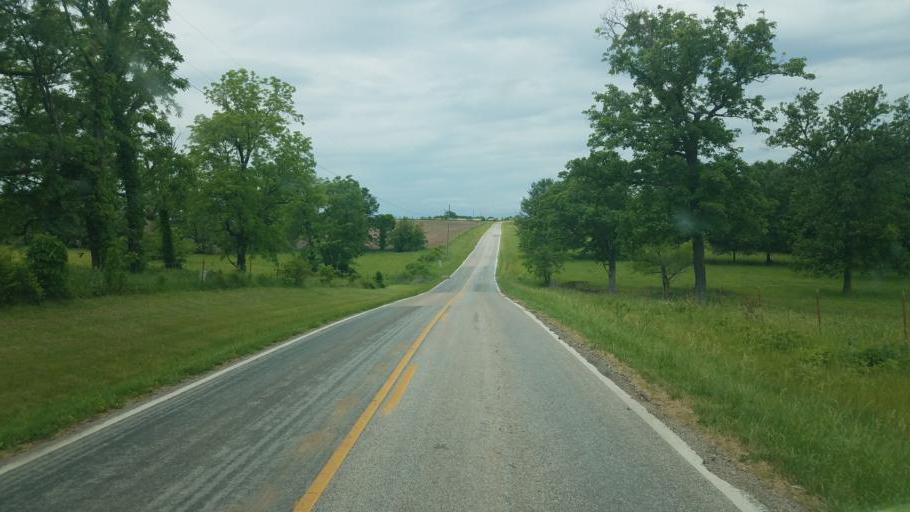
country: US
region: Missouri
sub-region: Moniteau County
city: California
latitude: 38.6670
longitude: -92.5844
